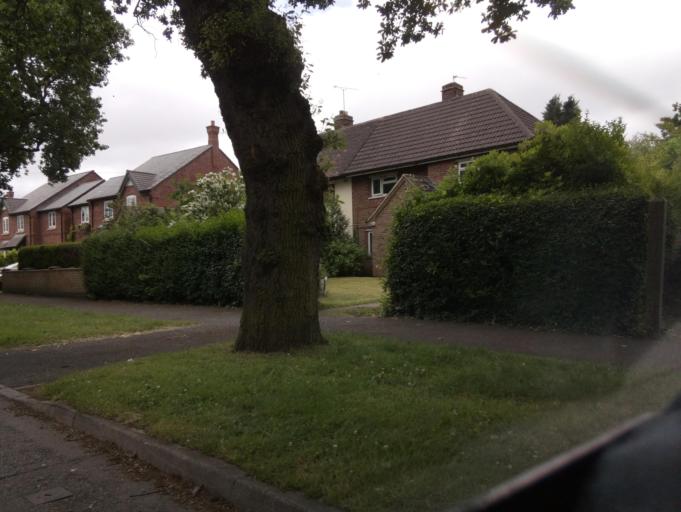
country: GB
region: England
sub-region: Leicestershire
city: Coalville
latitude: 52.7277
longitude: -1.3419
